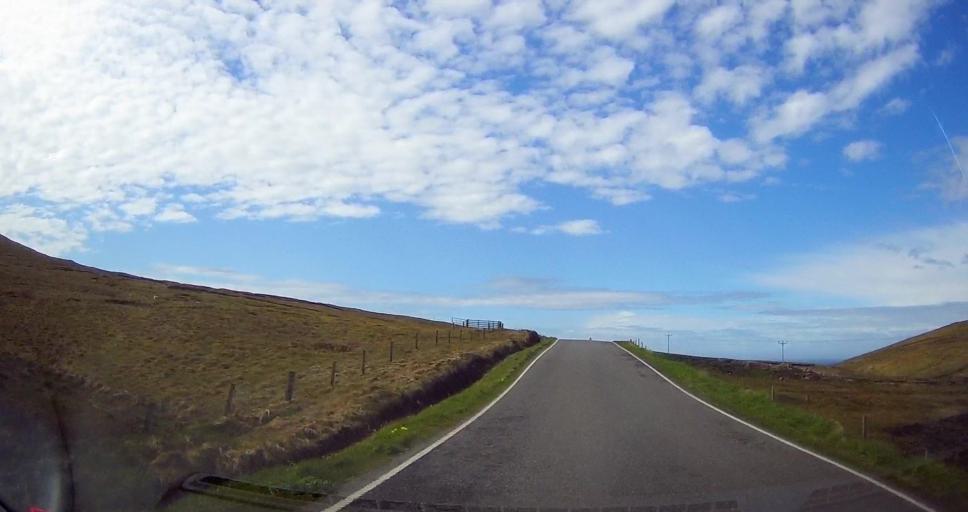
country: GB
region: Scotland
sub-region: Shetland Islands
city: Sandwick
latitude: 59.9806
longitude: -1.2924
